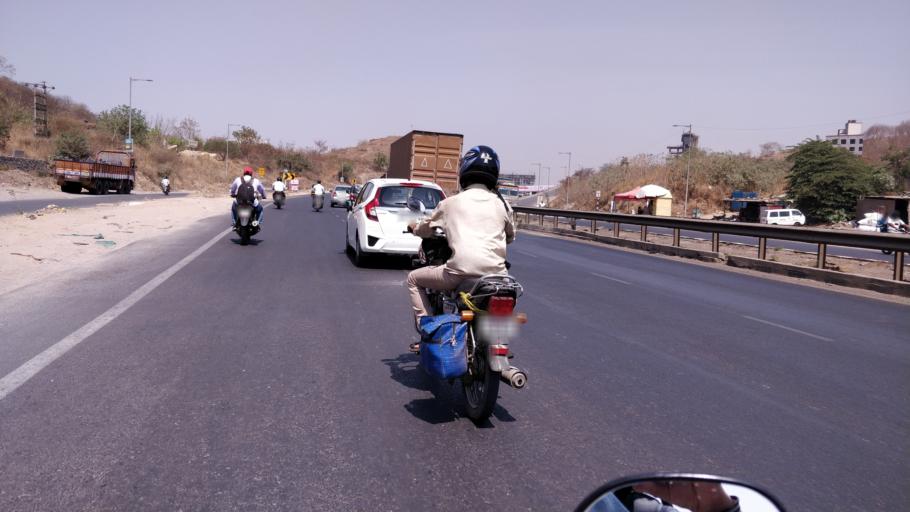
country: IN
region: Maharashtra
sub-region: Pune Division
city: Shivaji Nagar
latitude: 18.5437
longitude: 73.7755
